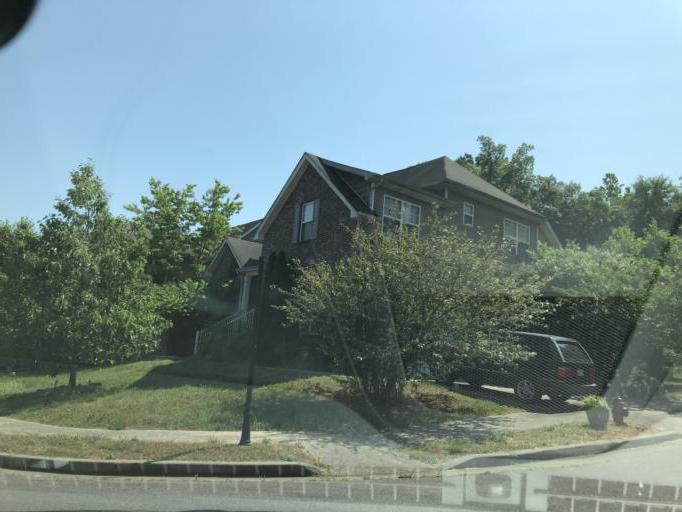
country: US
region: Tennessee
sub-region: Rutherford County
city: La Vergne
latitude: 36.0596
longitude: -86.6494
